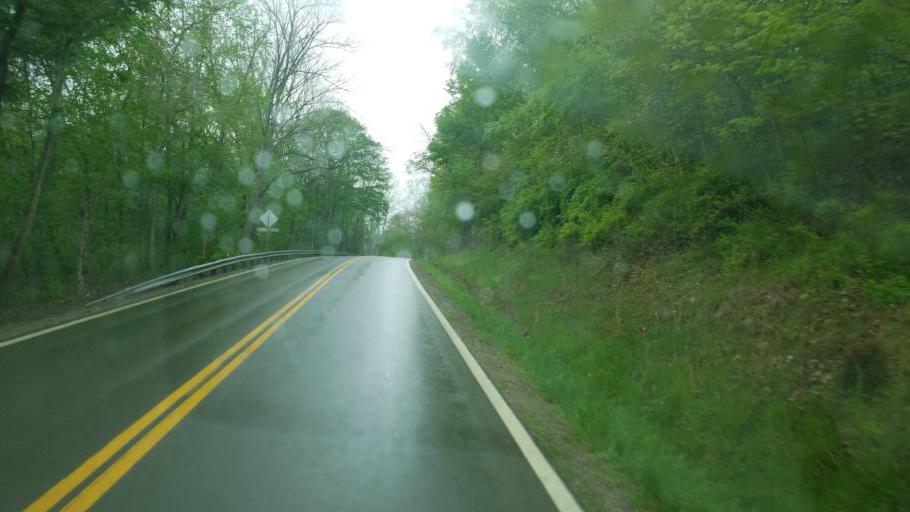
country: US
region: Ohio
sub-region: Muskingum County
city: Dresden
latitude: 40.2132
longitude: -82.0586
